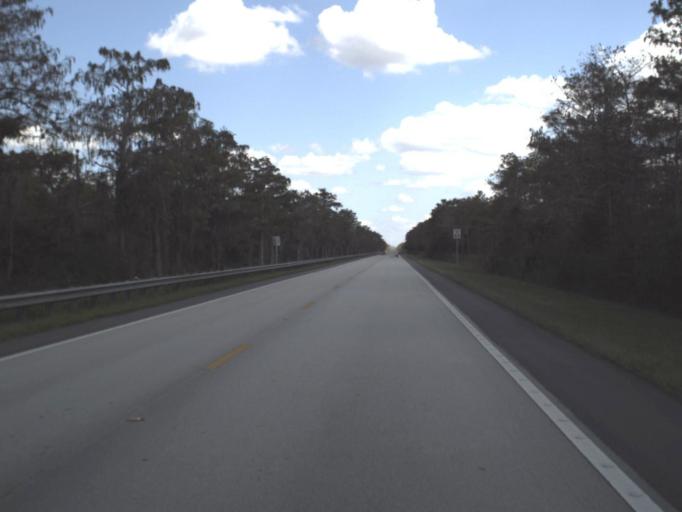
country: US
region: Florida
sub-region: Miami-Dade County
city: Kendall West
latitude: 25.8481
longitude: -80.9468
